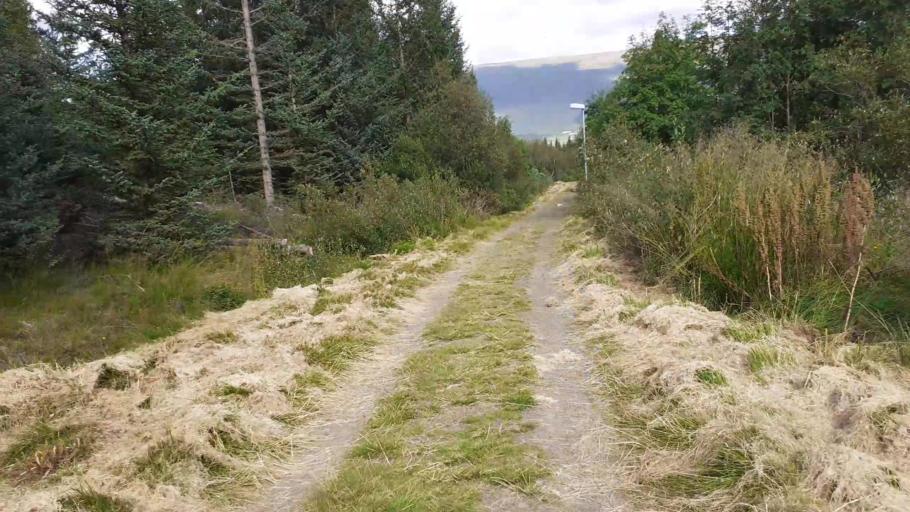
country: IS
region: Northeast
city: Akureyri
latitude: 65.6418
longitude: -18.0931
